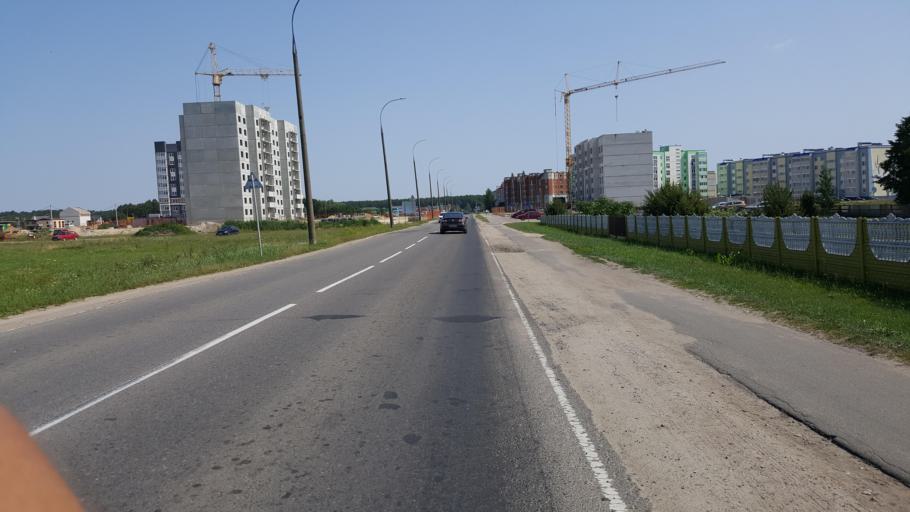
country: BY
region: Brest
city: Zhabinka
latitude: 52.1980
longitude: 24.0314
